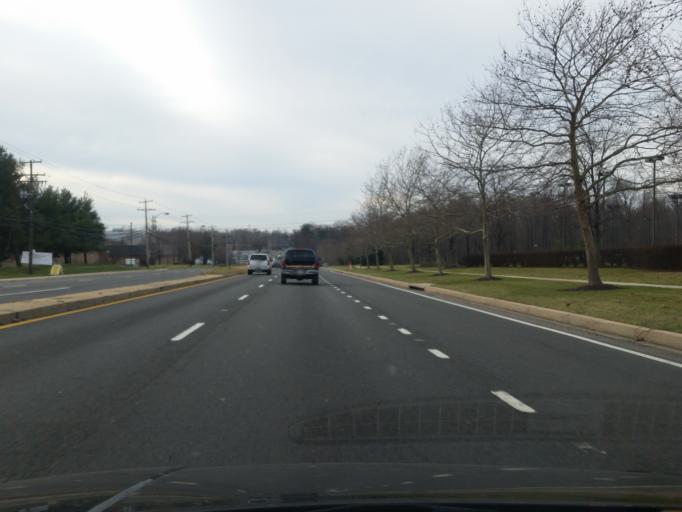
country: US
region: Maryland
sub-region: Howard County
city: Savage
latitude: 39.1267
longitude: -76.8225
